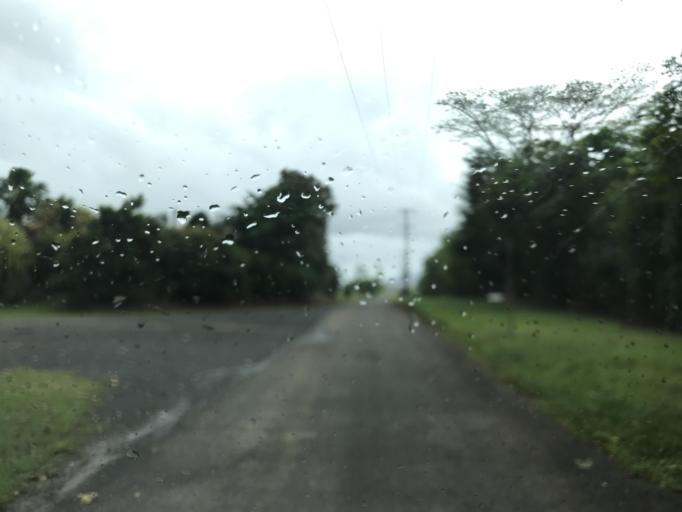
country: AU
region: Queensland
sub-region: Cassowary Coast
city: Innisfail
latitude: -17.4849
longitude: 145.9891
